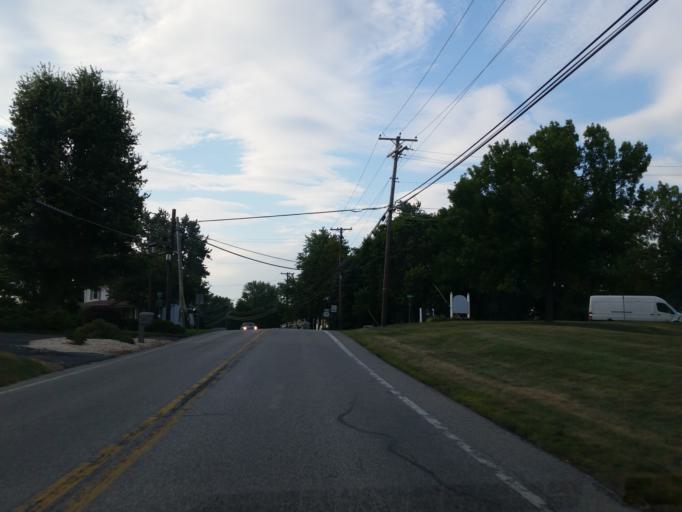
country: US
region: Pennsylvania
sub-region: Lebanon County
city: Palmyra
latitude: 40.2971
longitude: -76.5766
